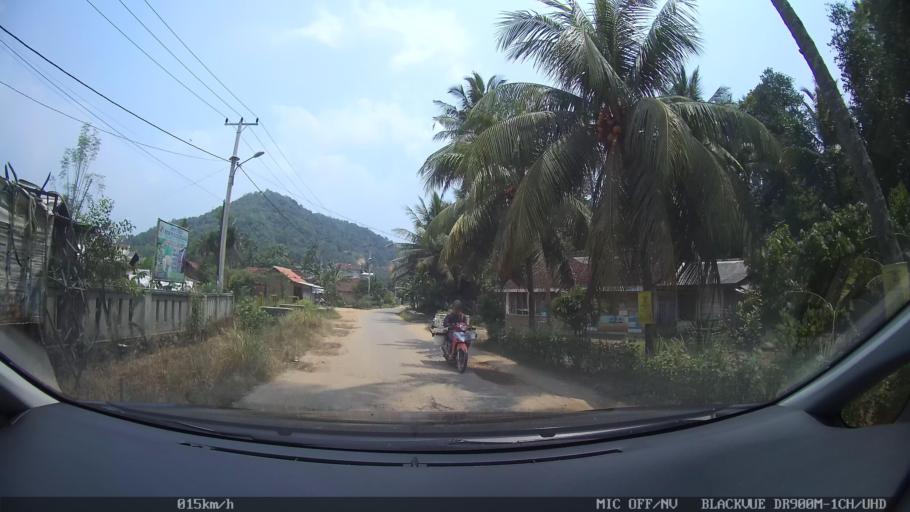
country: ID
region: Lampung
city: Pringsewu
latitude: -5.3779
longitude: 104.9998
